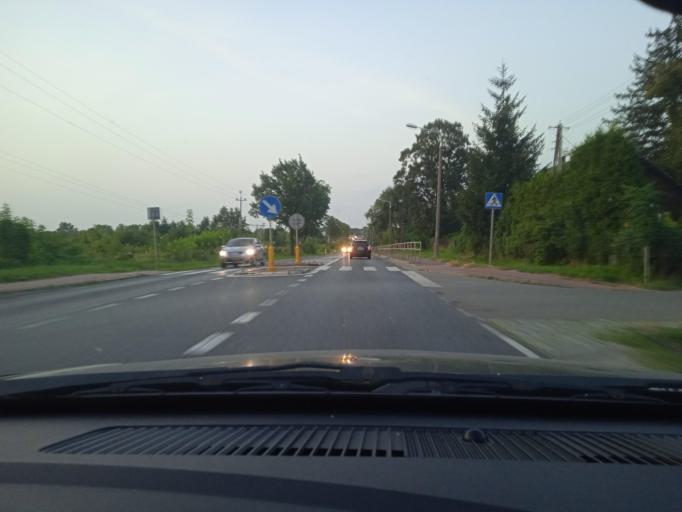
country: PL
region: Masovian Voivodeship
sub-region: Powiat nowodworski
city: Pomiechowek
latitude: 52.4576
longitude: 20.7156
